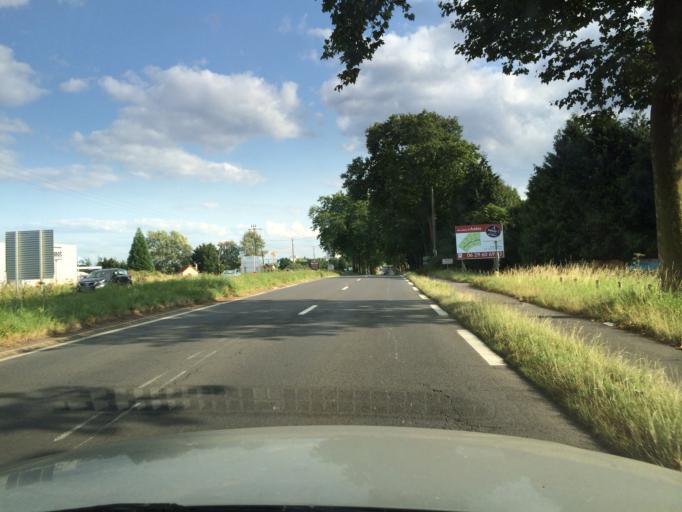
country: FR
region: Lower Normandy
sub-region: Departement du Calvados
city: Epron
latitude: 49.2276
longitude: -0.3704
